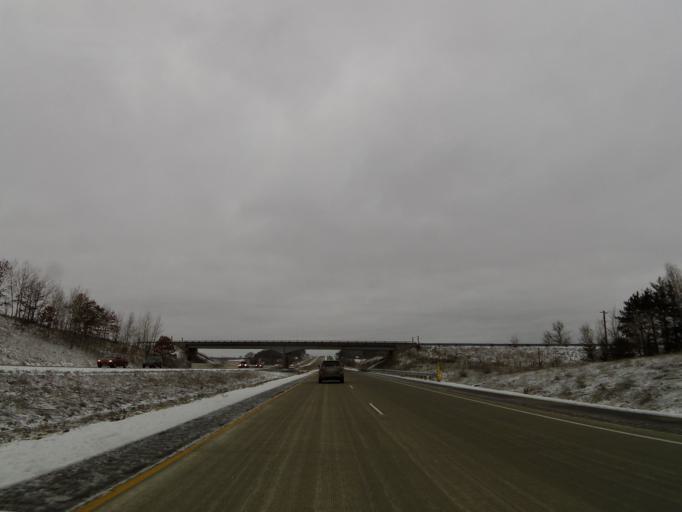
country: US
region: Wisconsin
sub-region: Trempealeau County
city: Osseo
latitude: 44.6257
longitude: -91.2771
